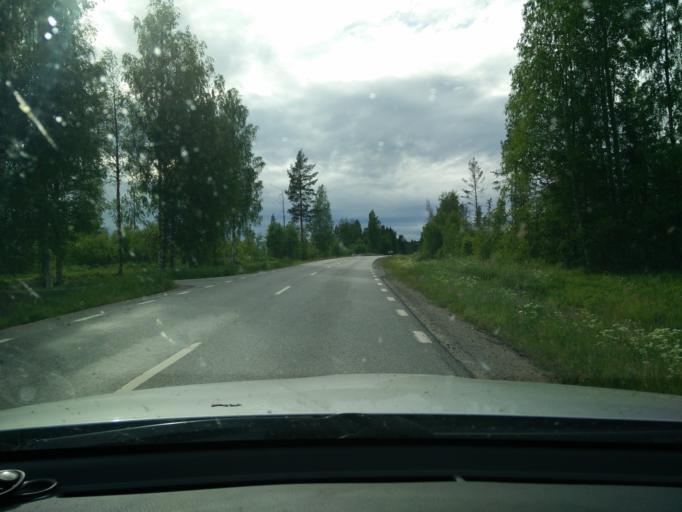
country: SE
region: Gaevleborg
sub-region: Nordanstigs Kommun
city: Bergsjoe
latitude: 62.0855
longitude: 16.7937
